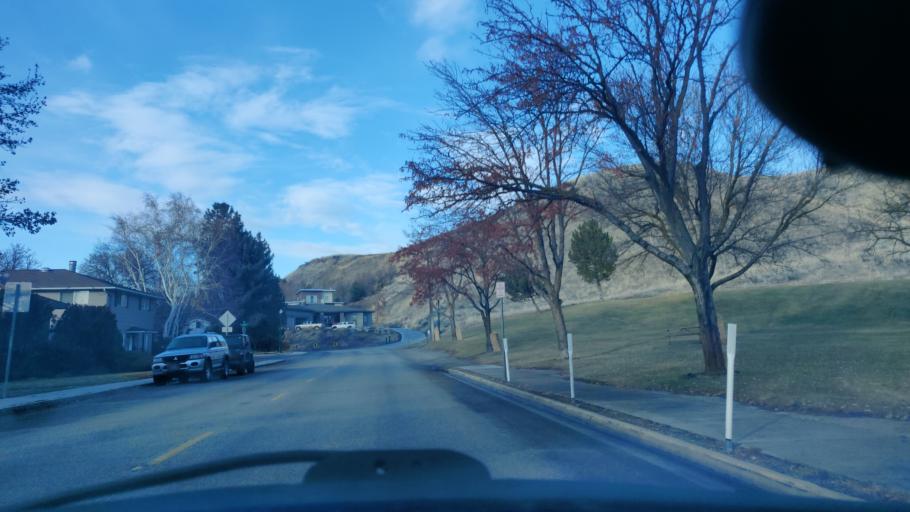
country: US
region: Idaho
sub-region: Ada County
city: Boise
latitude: 43.6357
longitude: -116.2033
